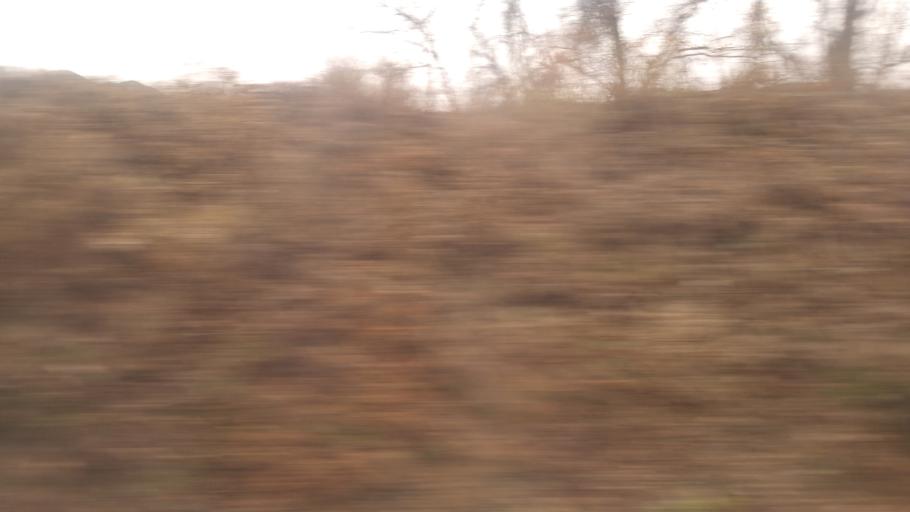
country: JP
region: Nagano
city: Ina
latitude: 35.8666
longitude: 137.7295
